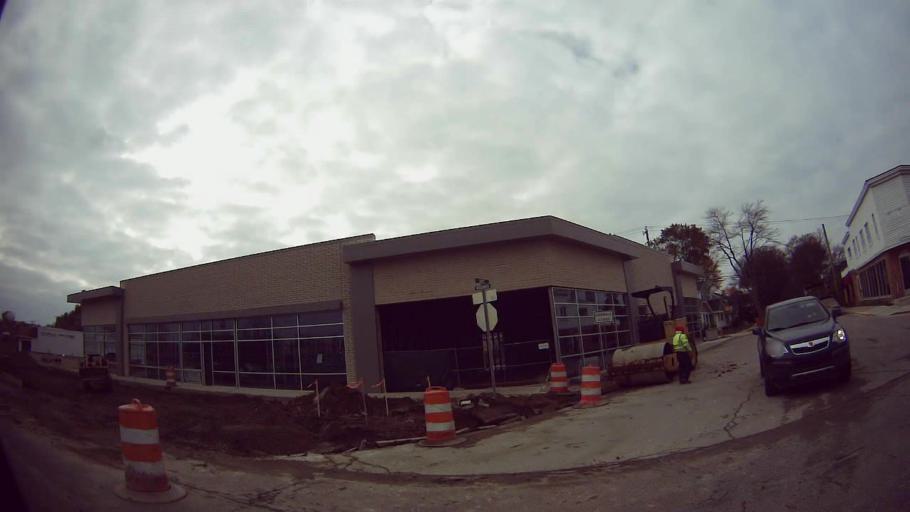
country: US
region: Michigan
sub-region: Oakland County
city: Birmingham
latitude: 42.5344
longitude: -83.2023
